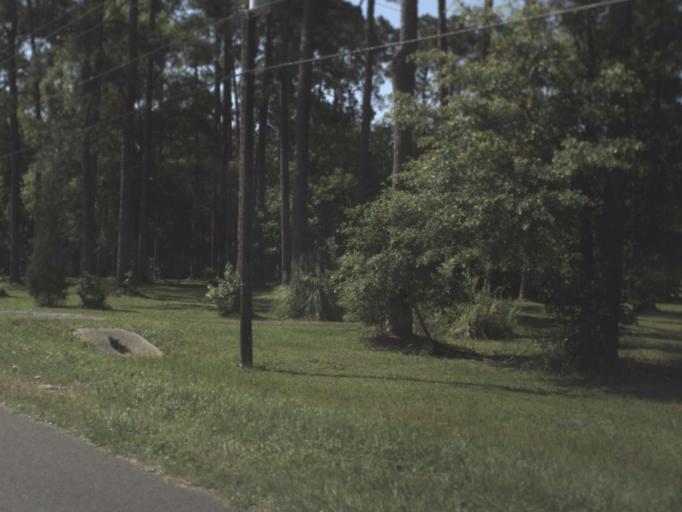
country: US
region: Florida
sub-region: Nassau County
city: Callahan
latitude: 30.5533
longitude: -81.8061
